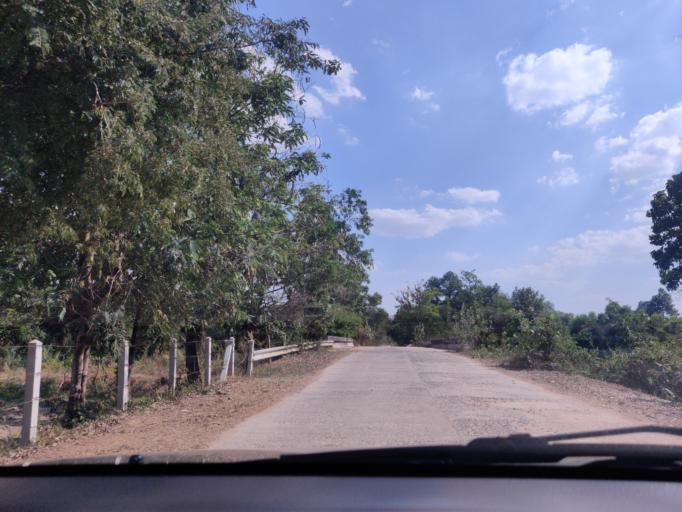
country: TH
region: Sisaket
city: Si Sa Ket
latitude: 15.0697
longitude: 104.3493
